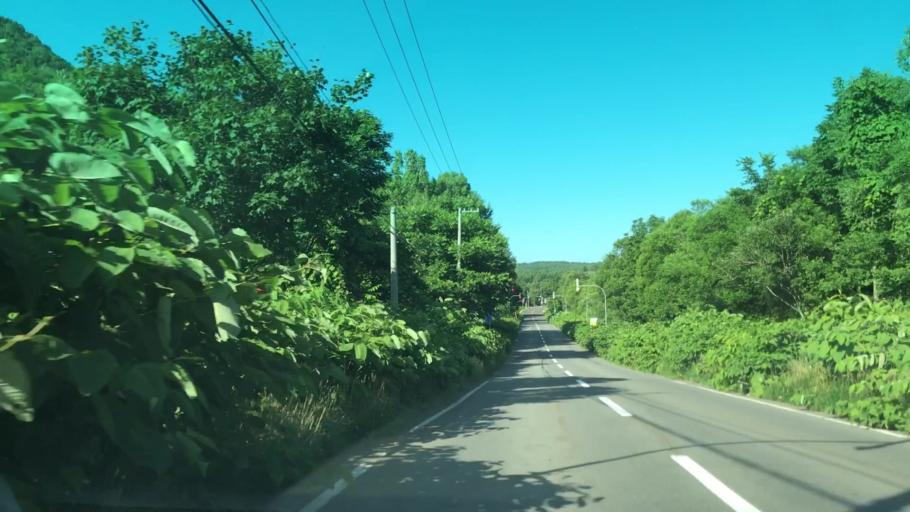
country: JP
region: Hokkaido
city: Yoichi
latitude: 43.0581
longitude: 140.8665
